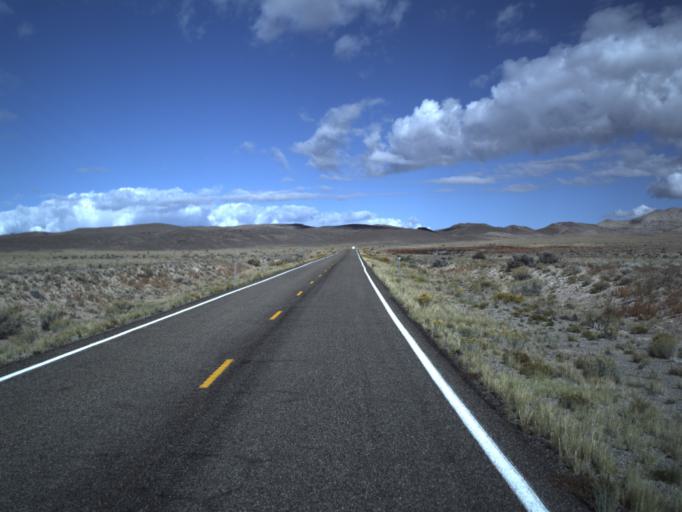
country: US
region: Utah
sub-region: Beaver County
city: Milford
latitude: 38.5820
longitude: -113.8097
